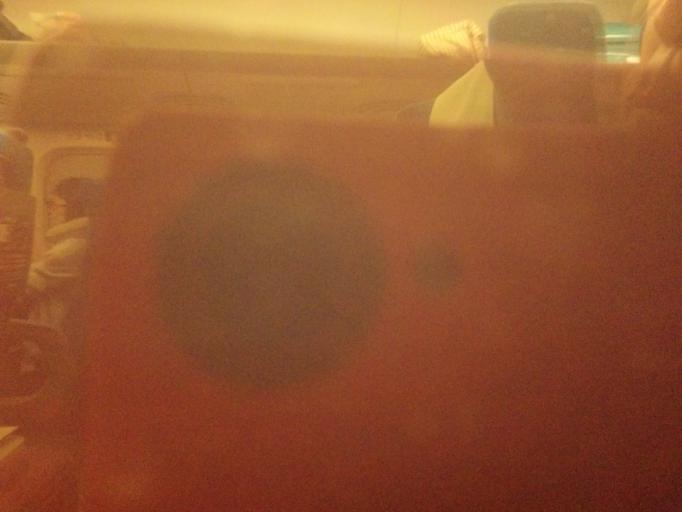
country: JP
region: Shizuoka
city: Atami
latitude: 35.1128
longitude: 139.0841
